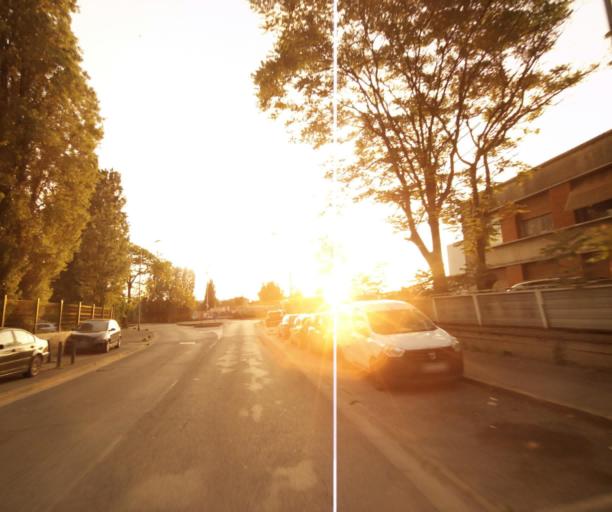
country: FR
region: Ile-de-France
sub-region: Departement des Hauts-de-Seine
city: Villeneuve-la-Garenne
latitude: 48.9326
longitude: 2.3137
